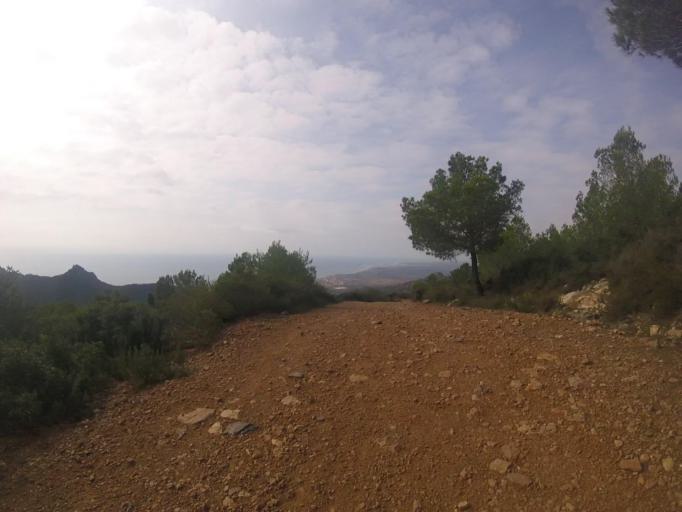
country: ES
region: Valencia
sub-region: Provincia de Castello
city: Benicassim
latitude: 40.0854
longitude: 0.0402
